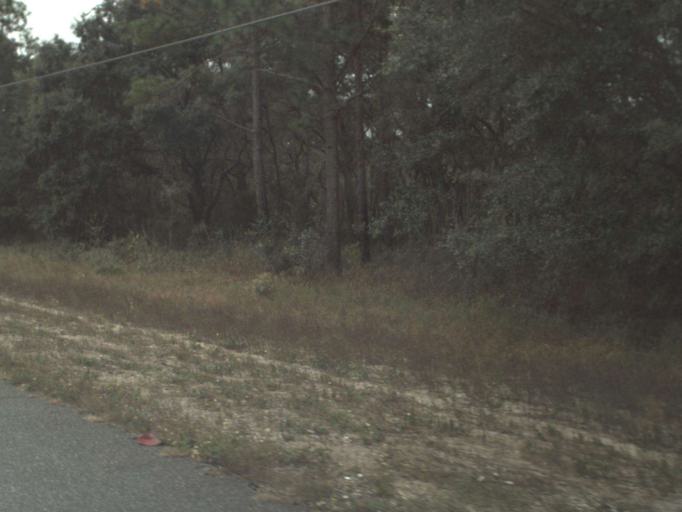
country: US
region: Florida
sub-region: Wakulla County
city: Crawfordville
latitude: 30.0554
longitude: -84.3883
